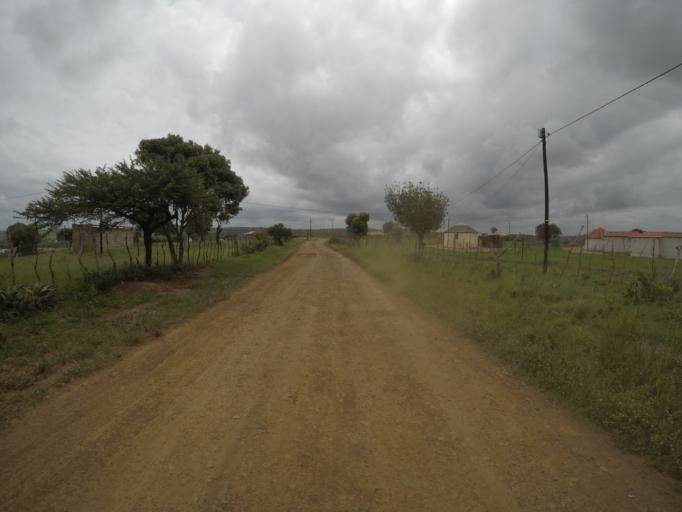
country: ZA
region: KwaZulu-Natal
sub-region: uThungulu District Municipality
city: Empangeni
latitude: -28.5996
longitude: 31.8328
